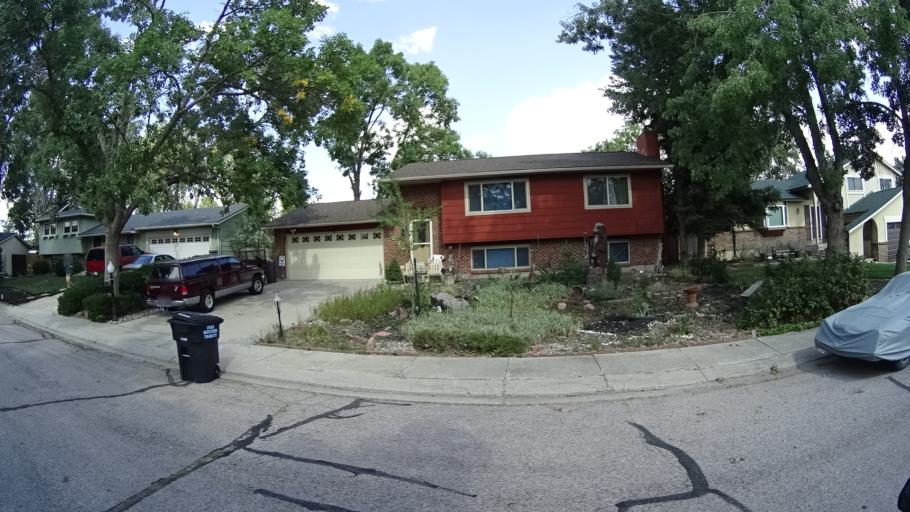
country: US
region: Colorado
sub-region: El Paso County
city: Cimarron Hills
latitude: 38.8761
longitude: -104.7348
